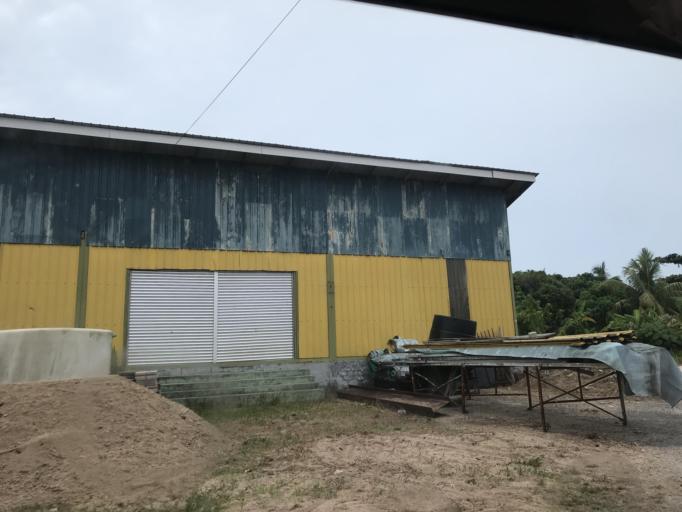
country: MY
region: Kelantan
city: Kota Bharu
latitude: 6.1182
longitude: 102.2064
